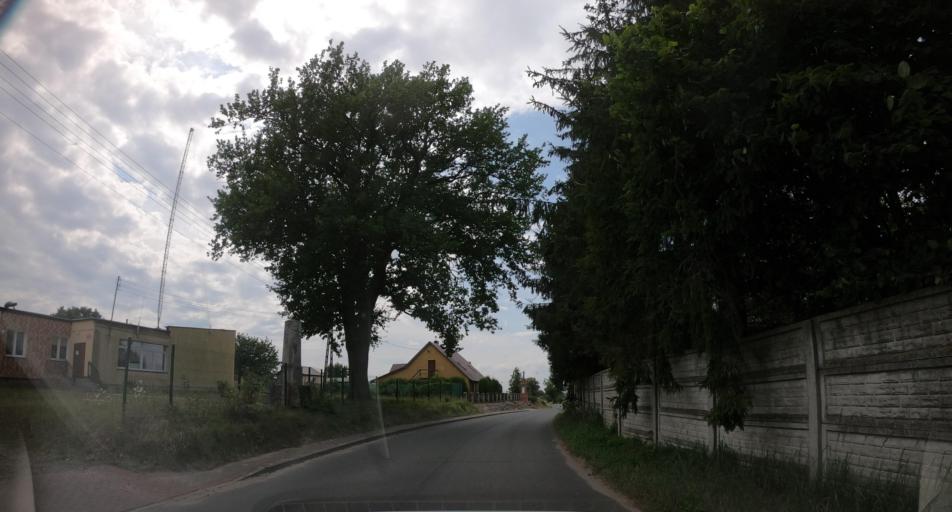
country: PL
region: West Pomeranian Voivodeship
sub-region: Powiat walecki
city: Tuczno
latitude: 53.2196
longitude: 16.2063
